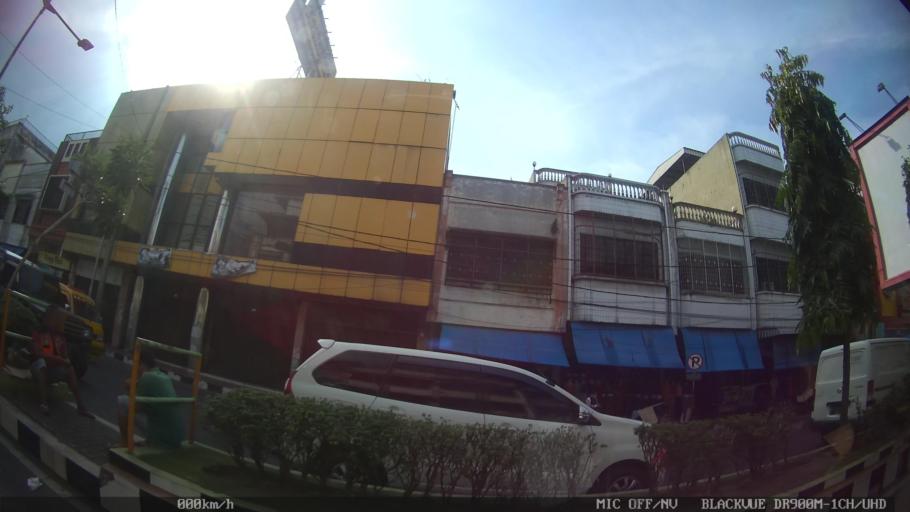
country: ID
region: North Sumatra
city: Binjai
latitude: 3.6090
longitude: 98.4905
